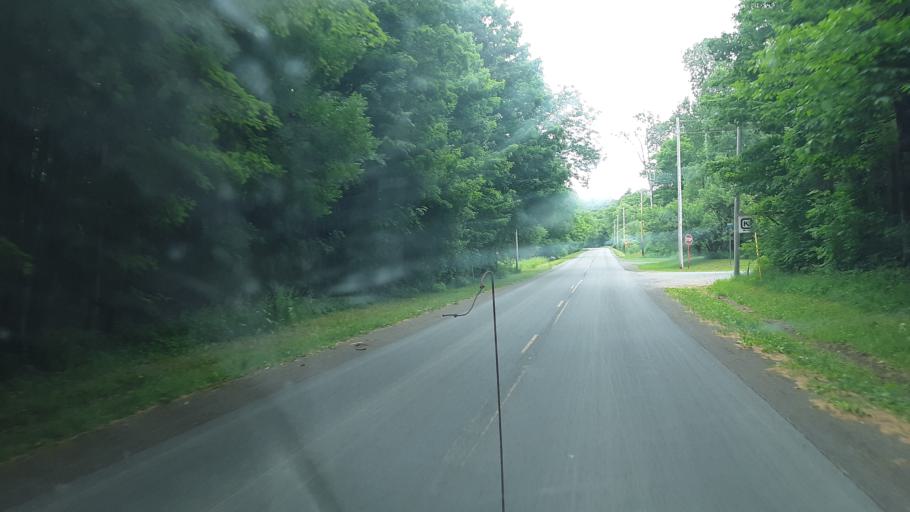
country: US
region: New York
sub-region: Oneida County
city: Rome
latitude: 43.4008
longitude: -75.5352
